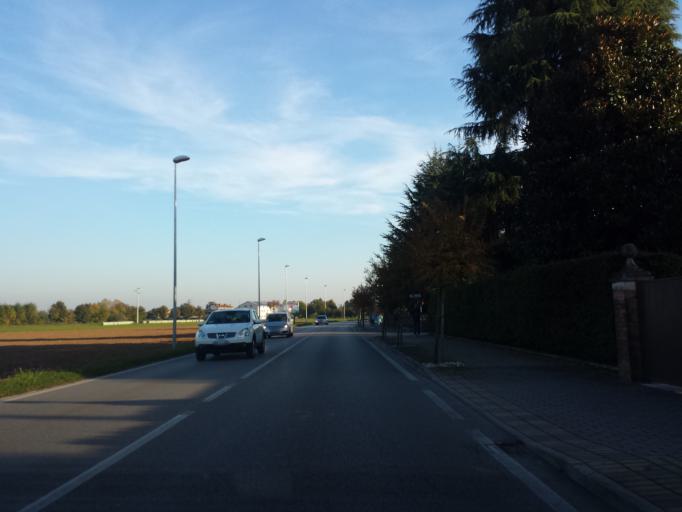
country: IT
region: Veneto
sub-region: Provincia di Vicenza
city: Crispi Cavour
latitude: 45.5885
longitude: 11.5301
